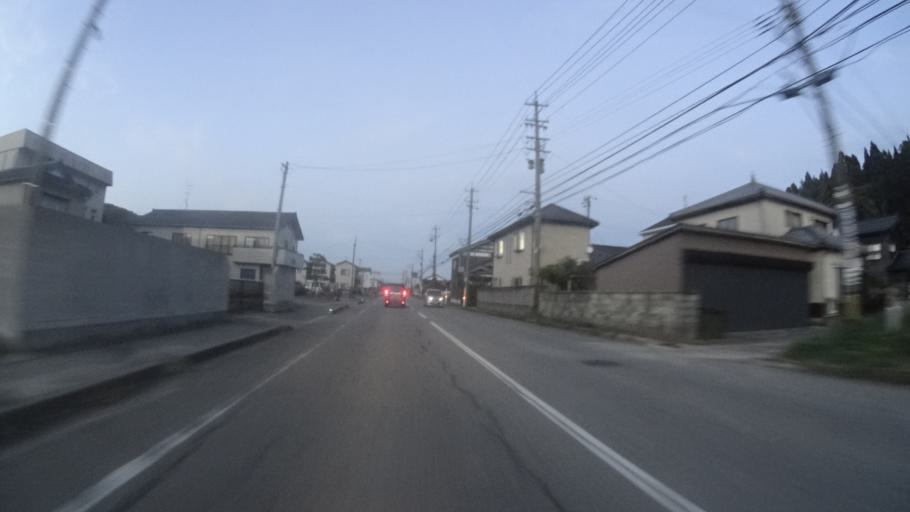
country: JP
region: Ishikawa
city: Nanao
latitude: 37.3798
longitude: 136.8854
